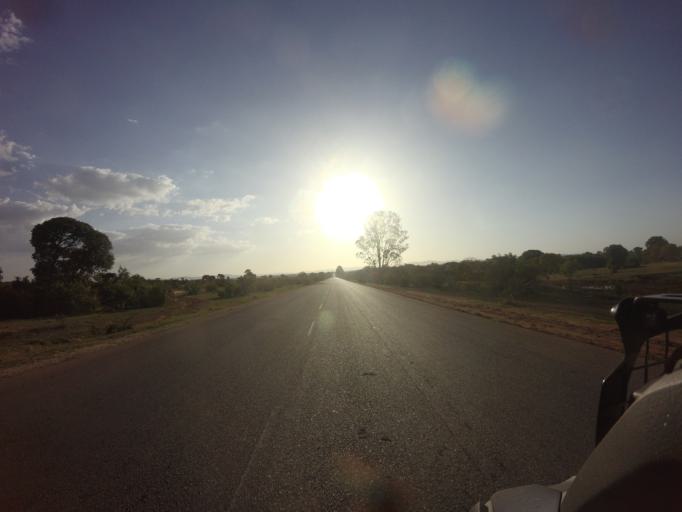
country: AO
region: Huila
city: Lubango
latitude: -14.8050
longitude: 13.6654
